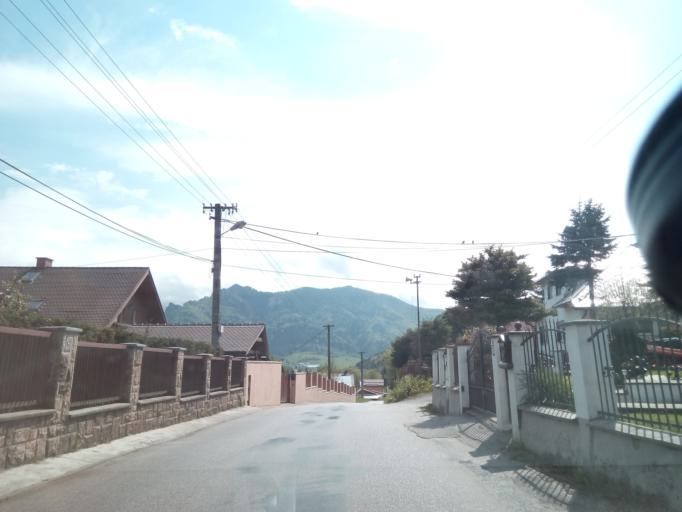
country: SK
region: Zilinsky
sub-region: Okres Zilina
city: Terchova
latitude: 49.2748
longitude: 19.0398
